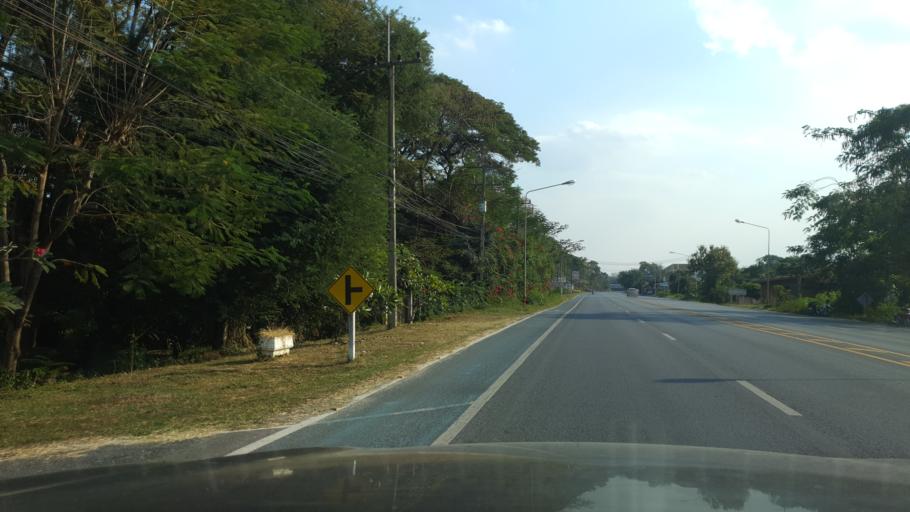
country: TH
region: Tak
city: Tak
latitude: 16.8632
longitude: 99.1206
